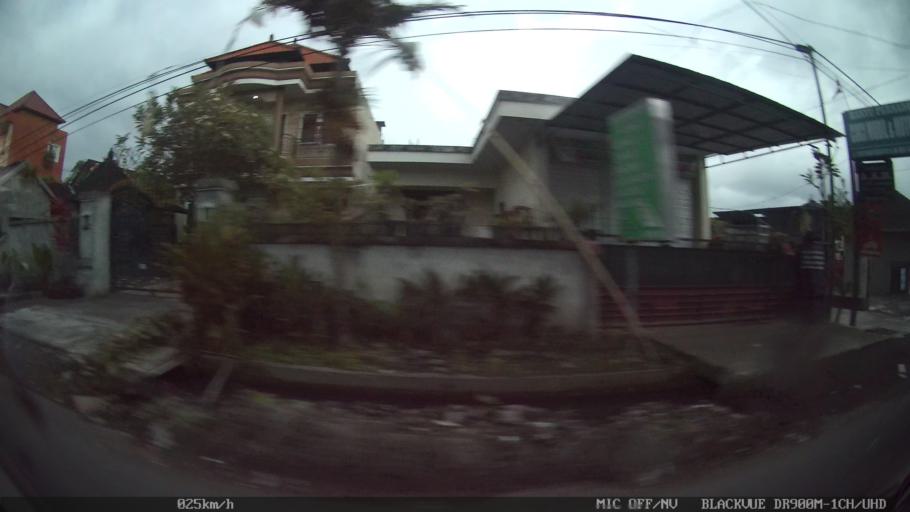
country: ID
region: Bali
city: Banjar Kertajiwa
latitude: -8.6399
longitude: 115.2685
